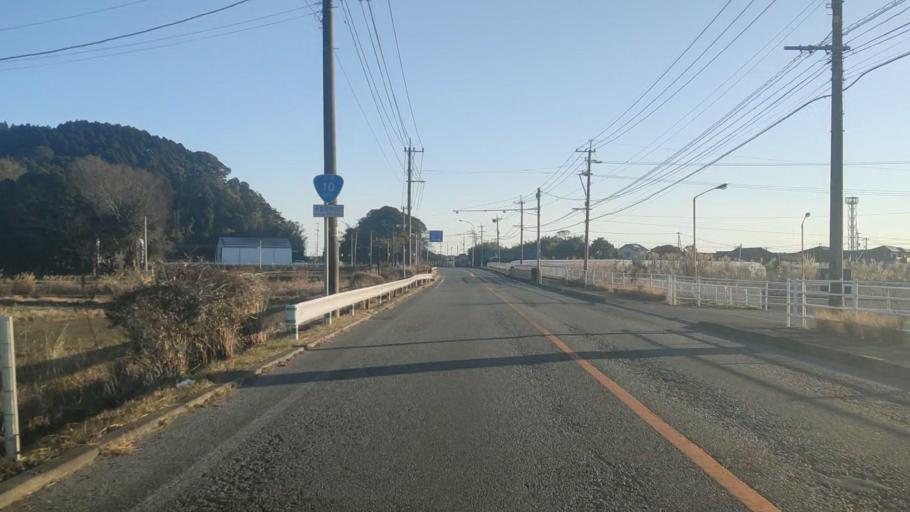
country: JP
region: Miyazaki
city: Takanabe
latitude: 32.0770
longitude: 131.5048
